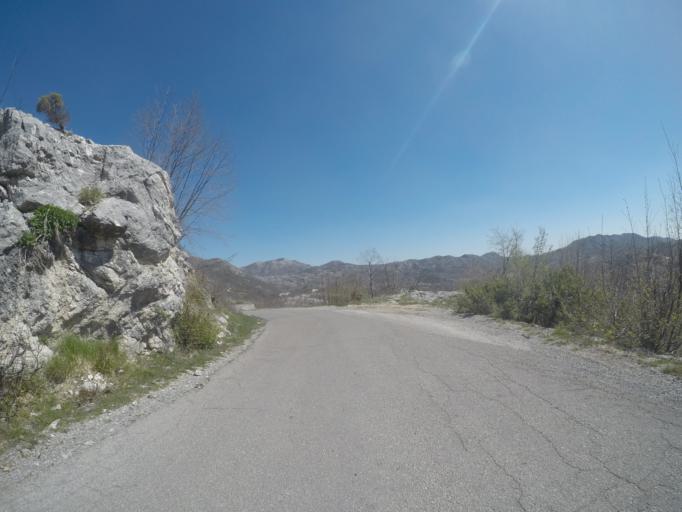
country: ME
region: Cetinje
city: Cetinje
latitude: 42.4368
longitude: 18.8700
